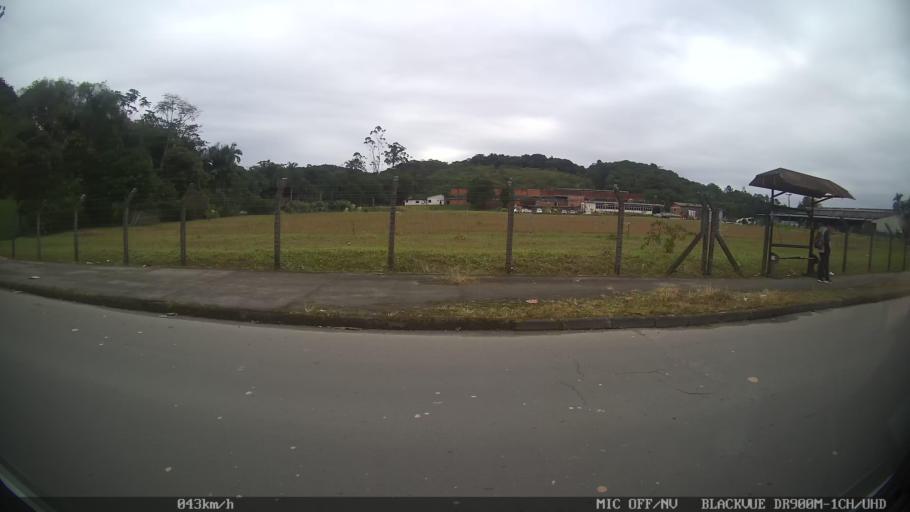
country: BR
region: Santa Catarina
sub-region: Joinville
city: Joinville
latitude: -26.2645
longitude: -48.8878
